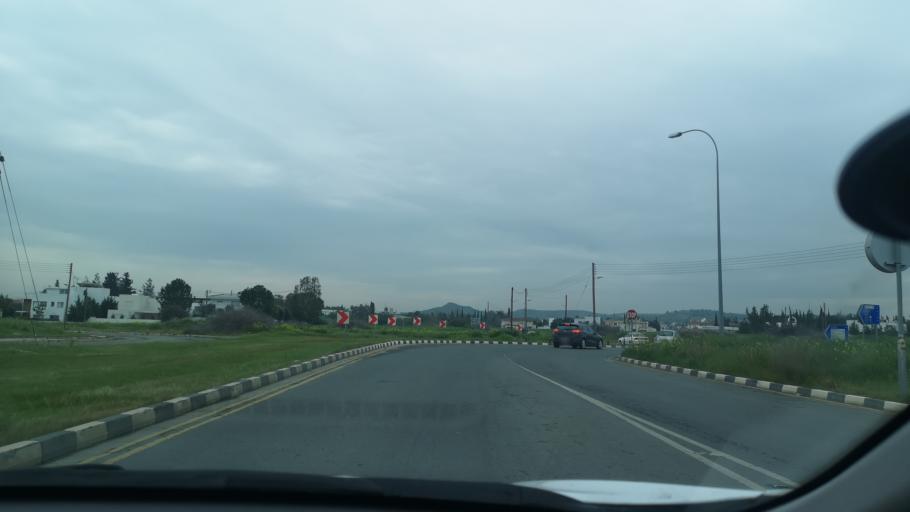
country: CY
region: Lefkosia
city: Tseri
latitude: 35.1103
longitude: 33.3554
